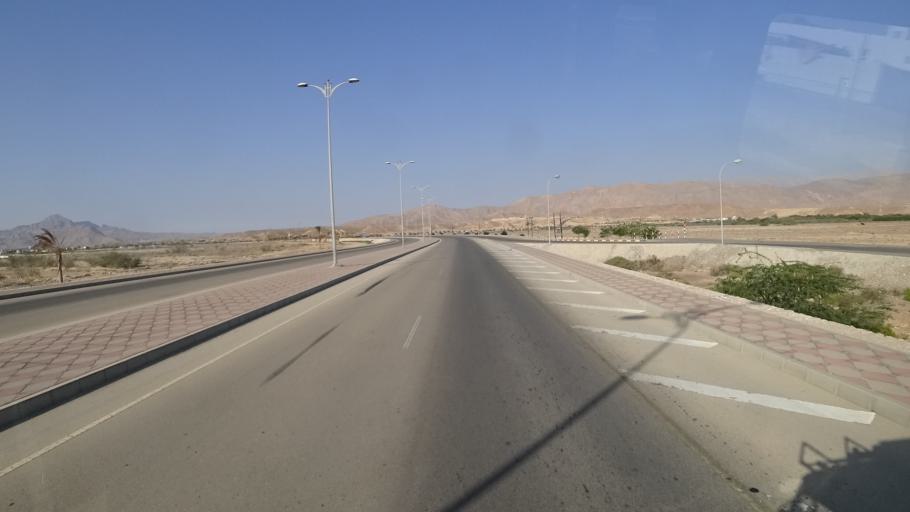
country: OM
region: Ash Sharqiyah
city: Sur
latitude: 22.5820
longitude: 59.4718
